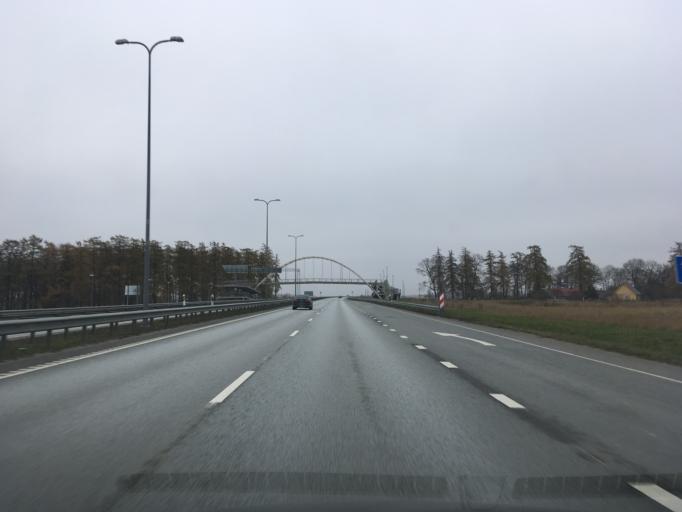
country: EE
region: Ida-Virumaa
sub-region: Johvi vald
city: Johvi
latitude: 59.3847
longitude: 27.3553
